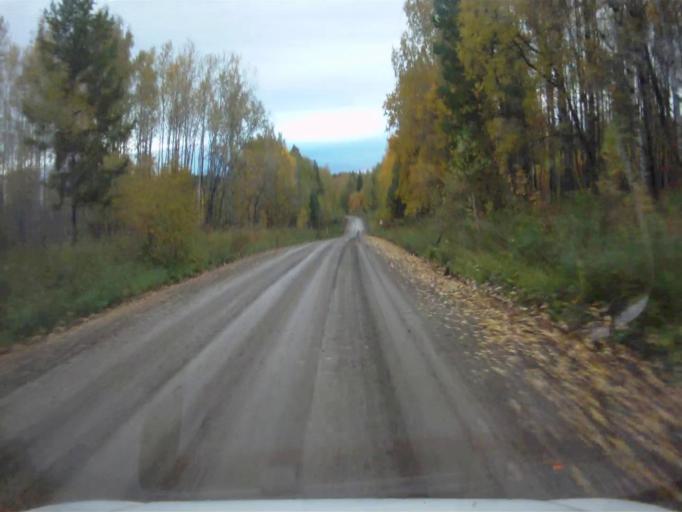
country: RU
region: Chelyabinsk
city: Nyazepetrovsk
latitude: 56.1168
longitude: 59.3682
